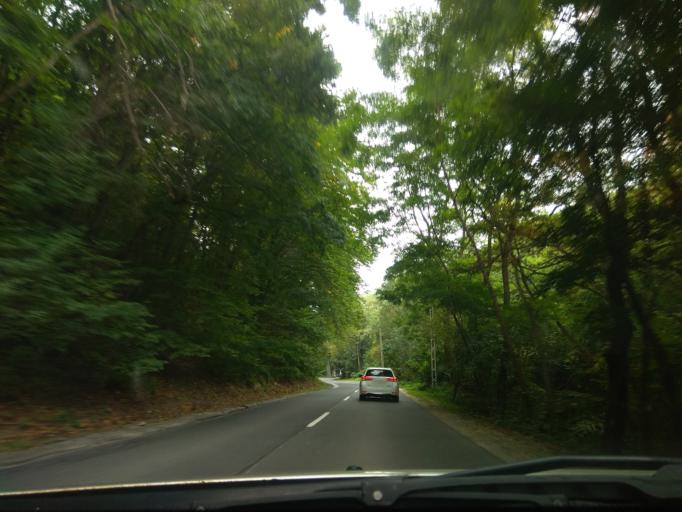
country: HU
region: Borsod-Abauj-Zemplen
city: Miskolc
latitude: 48.0805
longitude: 20.6982
